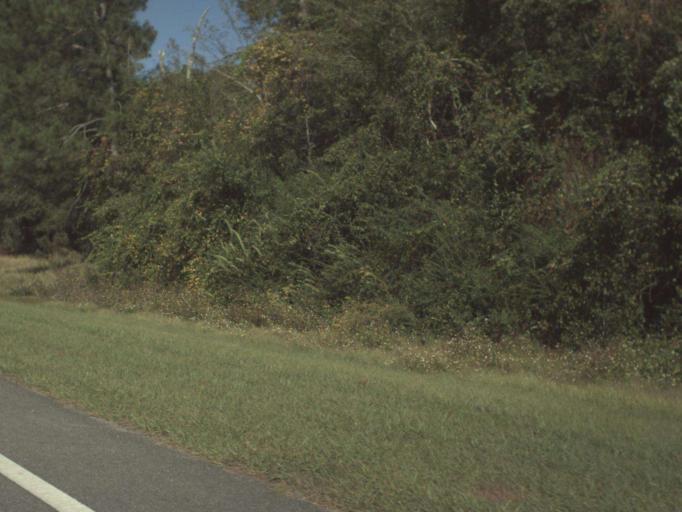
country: US
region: Florida
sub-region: Holmes County
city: Bonifay
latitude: 30.7890
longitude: -85.6939
